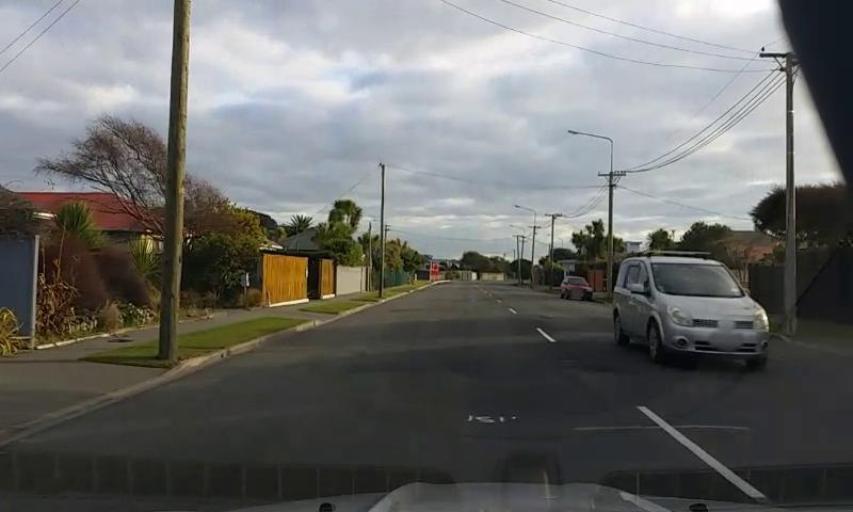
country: NZ
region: Canterbury
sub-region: Christchurch City
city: Christchurch
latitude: -43.5204
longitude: 172.7314
